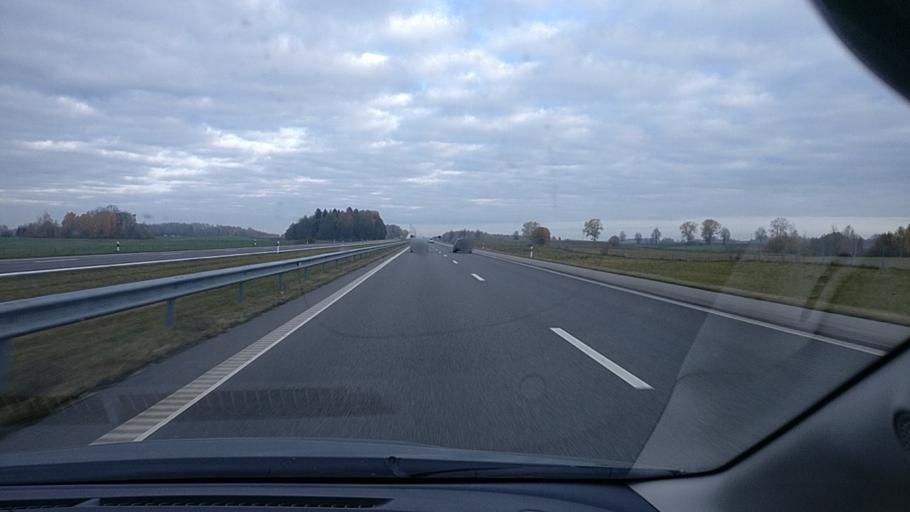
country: LT
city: Sirvintos
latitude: 55.1125
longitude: 24.8482
